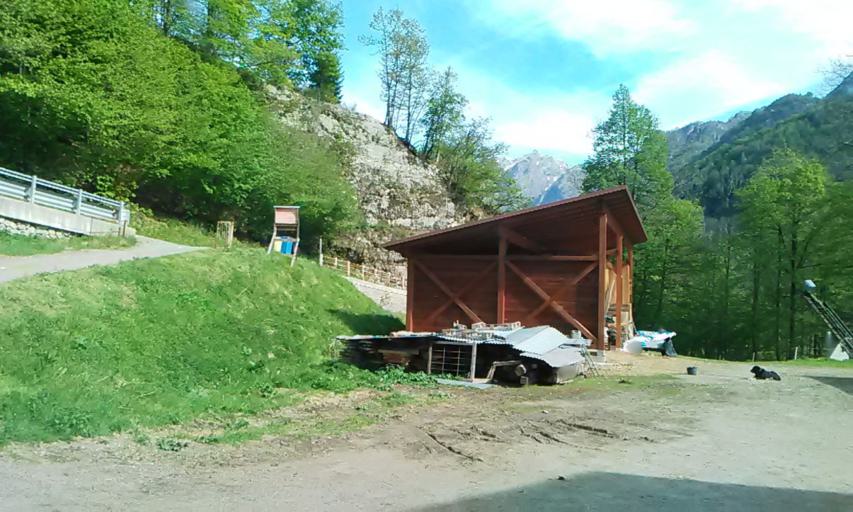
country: IT
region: Piedmont
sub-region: Provincia di Vercelli
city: Piode
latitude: 45.7772
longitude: 8.0421
